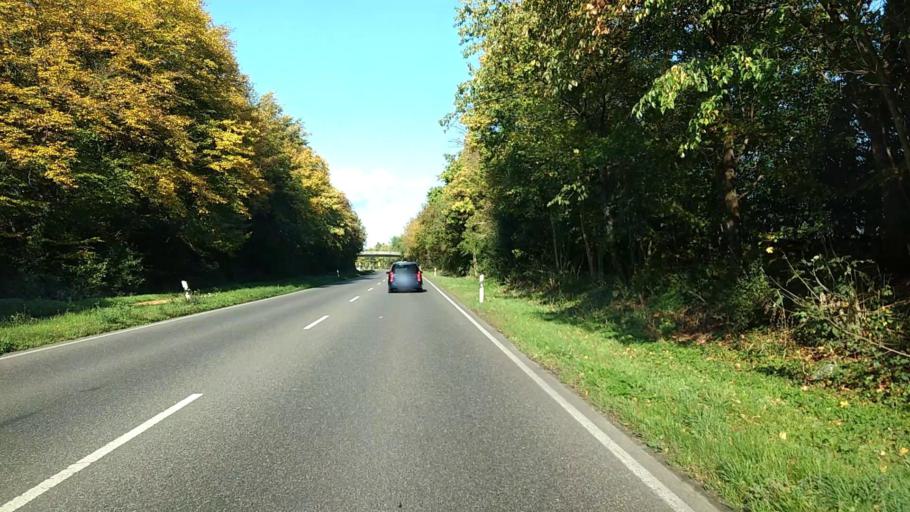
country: DE
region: North Rhine-Westphalia
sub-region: Regierungsbezirk Koln
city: Kerpen
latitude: 50.9060
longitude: 6.6844
